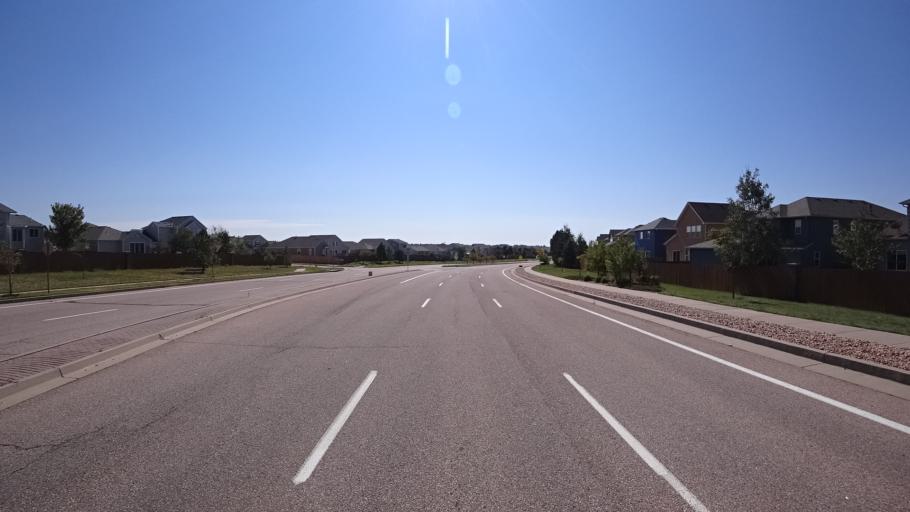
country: US
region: Colorado
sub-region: El Paso County
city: Cimarron Hills
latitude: 38.9284
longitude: -104.7005
